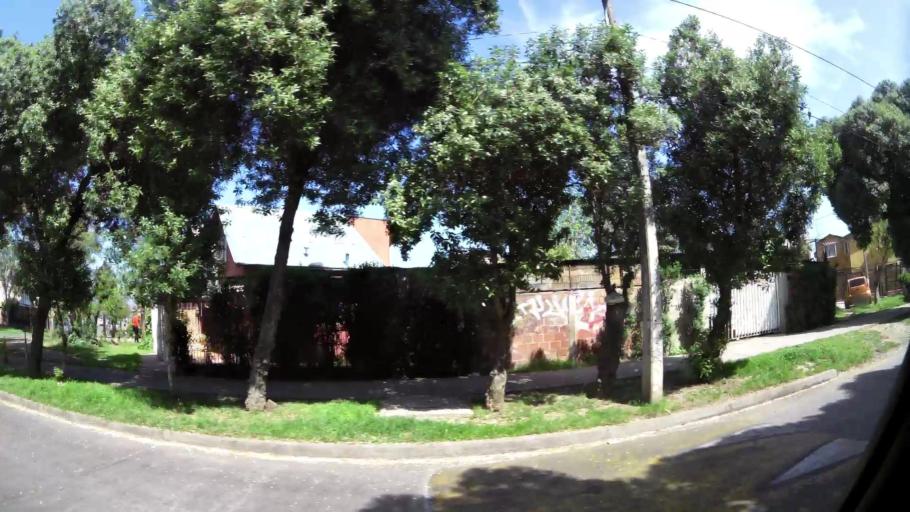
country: CL
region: Santiago Metropolitan
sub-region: Provincia de Santiago
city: Lo Prado
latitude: -33.4753
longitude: -70.7198
